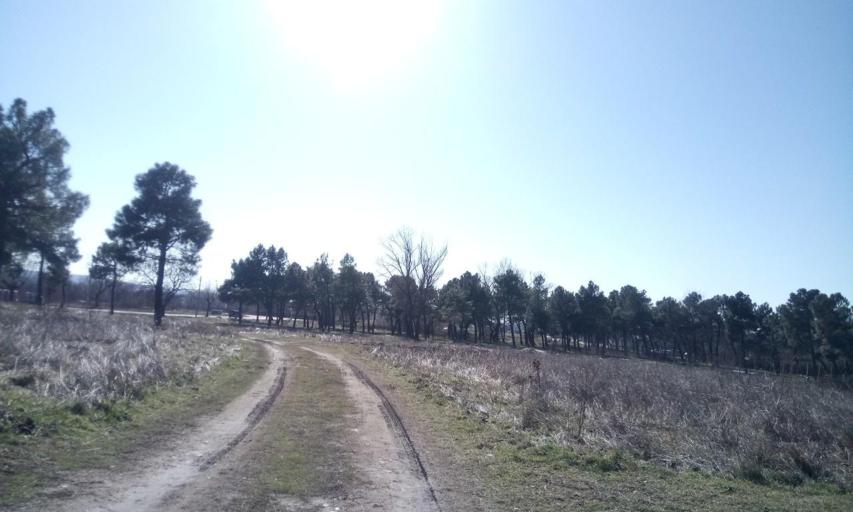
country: BG
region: Plovdiv
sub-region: Obshtina Khisarya
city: Khisarya
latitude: 42.5176
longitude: 24.7212
